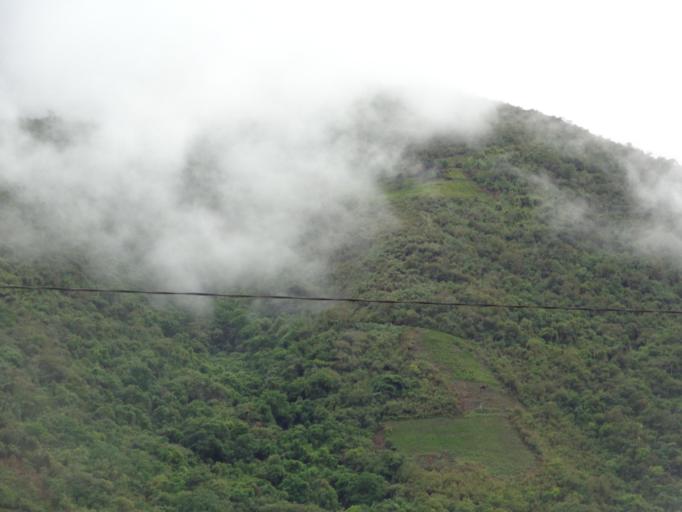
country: BO
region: La Paz
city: Coripata
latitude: -16.3931
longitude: -67.6807
